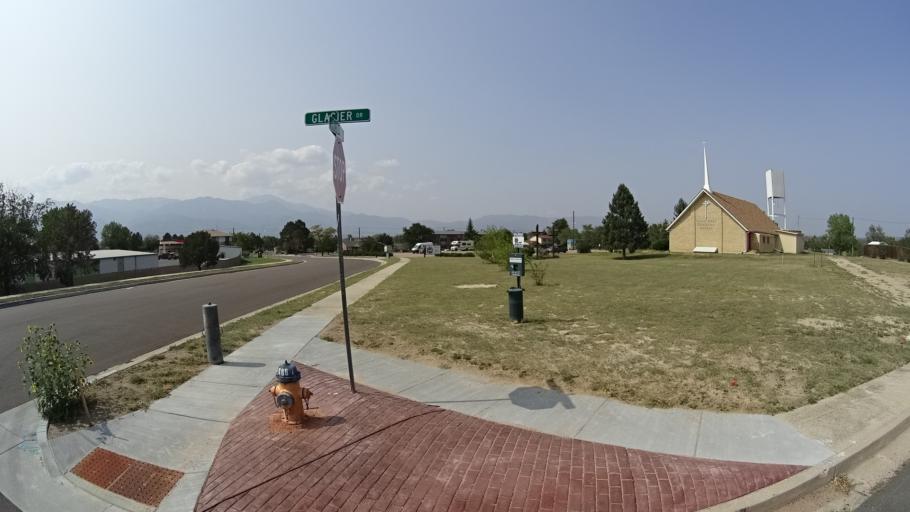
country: US
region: Colorado
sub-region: El Paso County
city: Stratmoor
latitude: 38.8080
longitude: -104.7777
